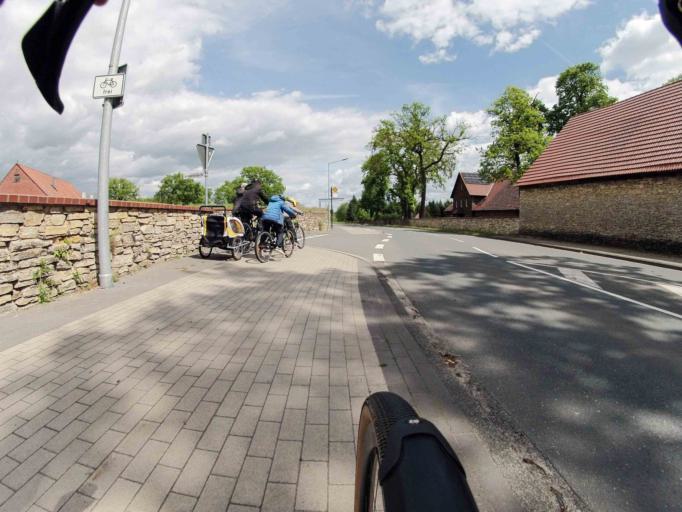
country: DE
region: North Rhine-Westphalia
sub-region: Regierungsbezirk Munster
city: Lotte
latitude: 52.3350
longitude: 7.9453
